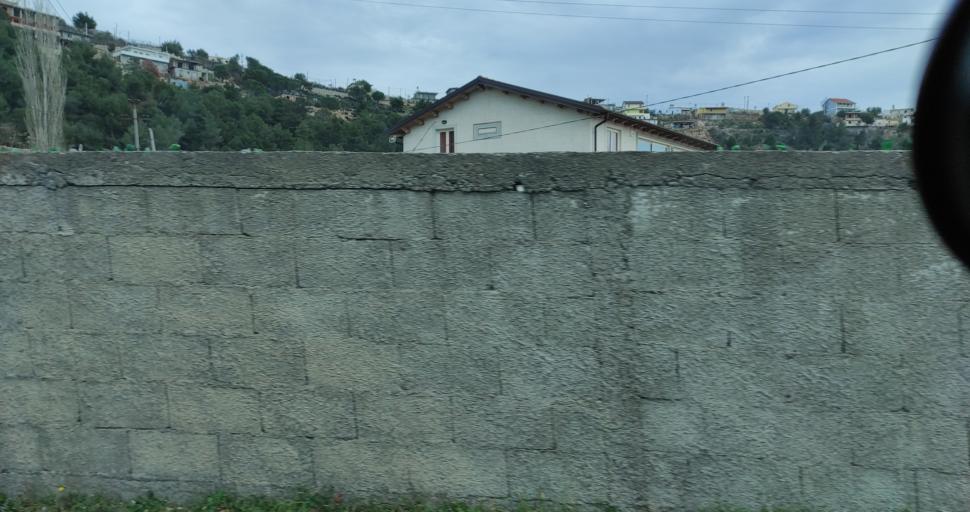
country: AL
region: Lezhe
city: Lezhe
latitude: 41.7869
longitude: 19.6281
